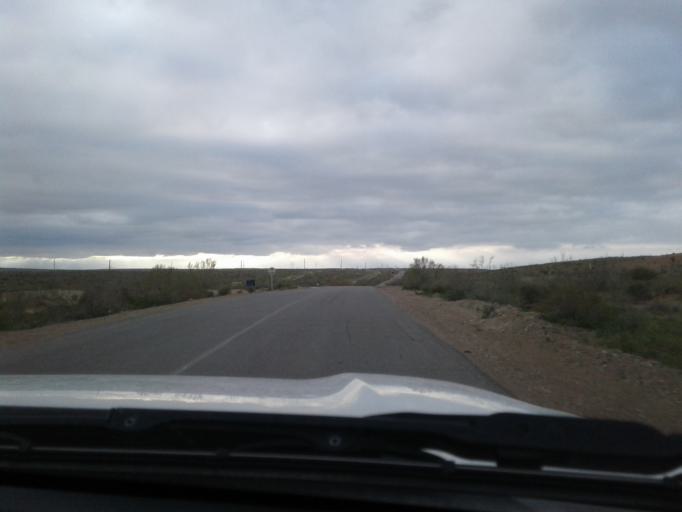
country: TM
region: Lebap
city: Sayat
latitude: 38.9166
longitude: 64.3026
